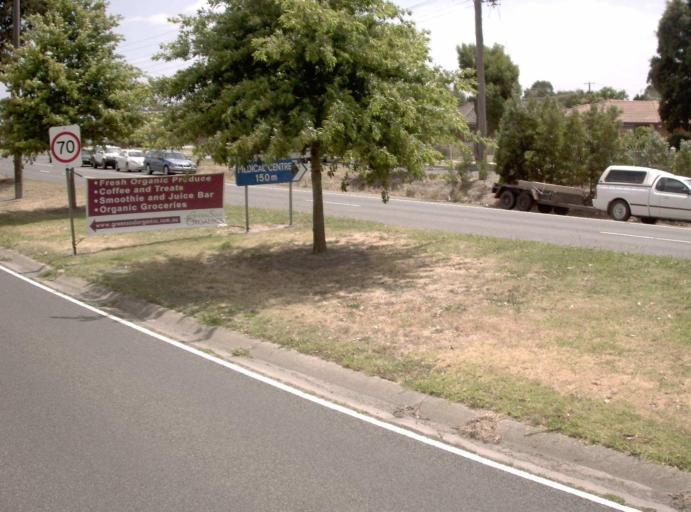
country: AU
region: Victoria
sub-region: Casey
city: Berwick
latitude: -38.0471
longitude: 145.3691
